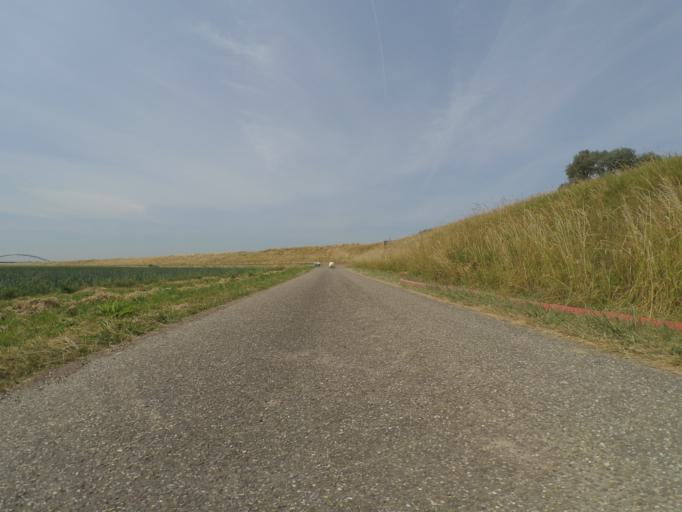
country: NL
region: North Brabant
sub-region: Gemeente Steenbergen
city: Nieuw-Vossemeer
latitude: 51.6196
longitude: 4.2029
